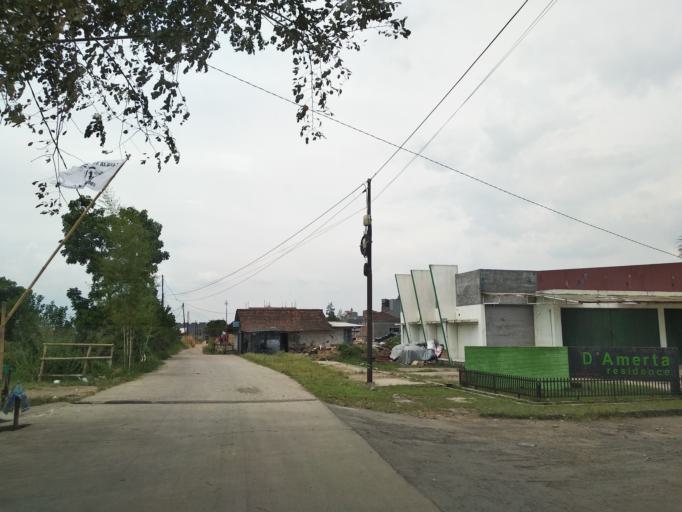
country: ID
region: West Java
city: Pameungpeuk
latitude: -6.9775
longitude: 107.6510
